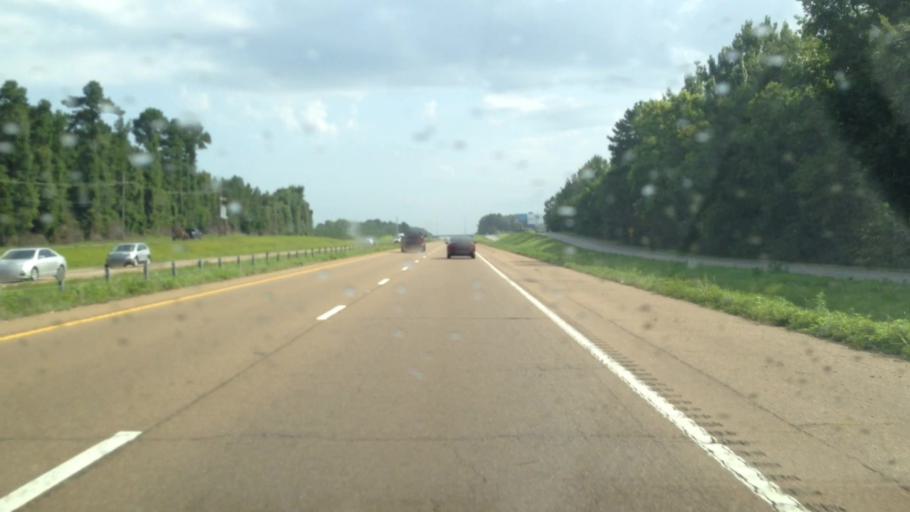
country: US
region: Mississippi
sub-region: Hinds County
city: Terry
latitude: 32.1200
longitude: -90.2930
